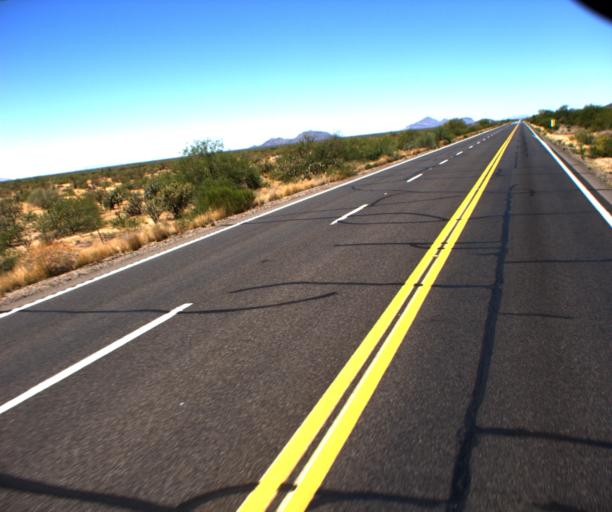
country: US
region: Arizona
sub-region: Yavapai County
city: Congress
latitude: 34.1476
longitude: -112.9852
